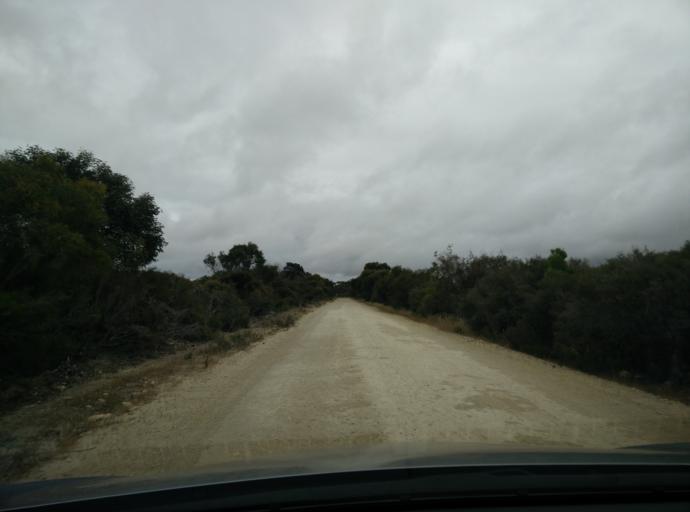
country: AU
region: South Australia
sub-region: Kangaroo Island
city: Kingscote
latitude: -35.8734
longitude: 137.4920
